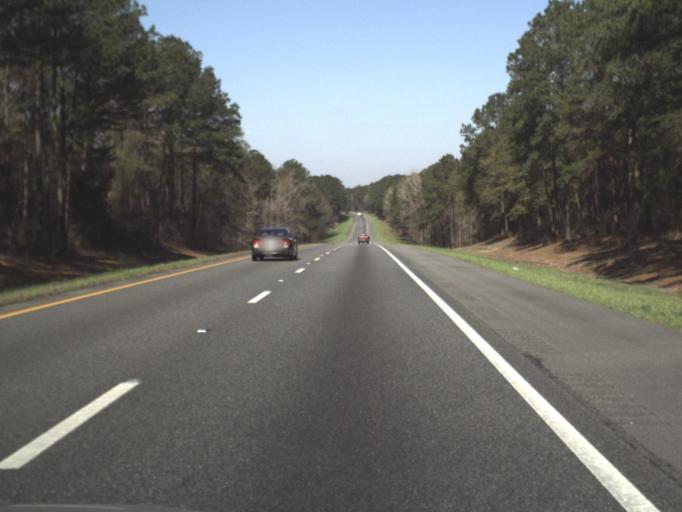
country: US
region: Florida
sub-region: Gadsden County
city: Midway
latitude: 30.5233
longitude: -84.4921
